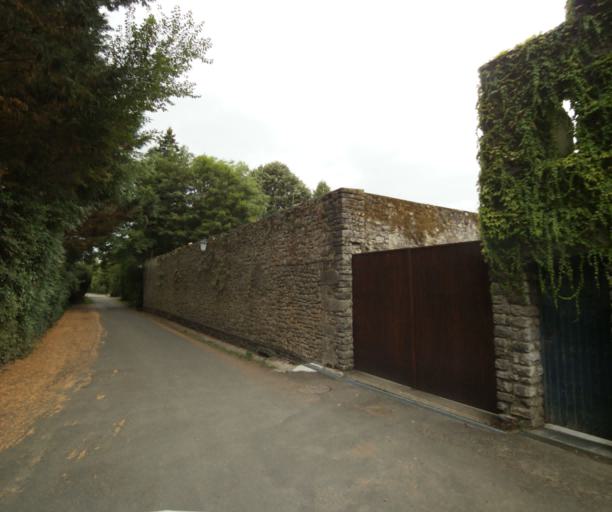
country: FR
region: Pays de la Loire
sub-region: Departement de la Sarthe
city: Solesmes
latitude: 47.8517
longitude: -0.3059
